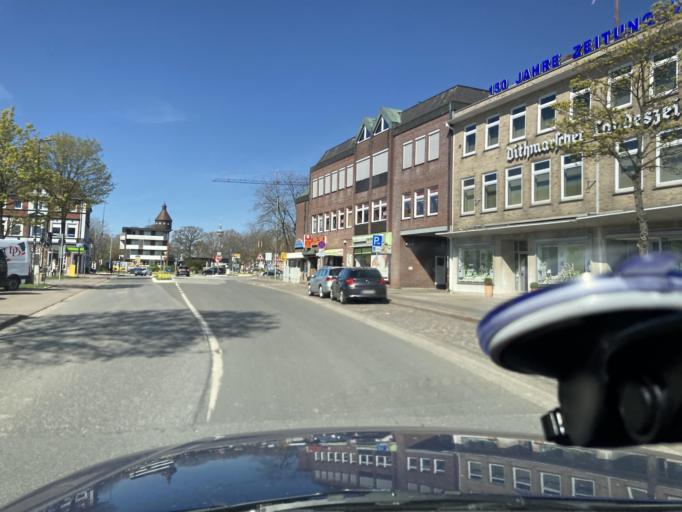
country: DE
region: Schleswig-Holstein
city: Heide
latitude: 54.1943
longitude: 9.0982
